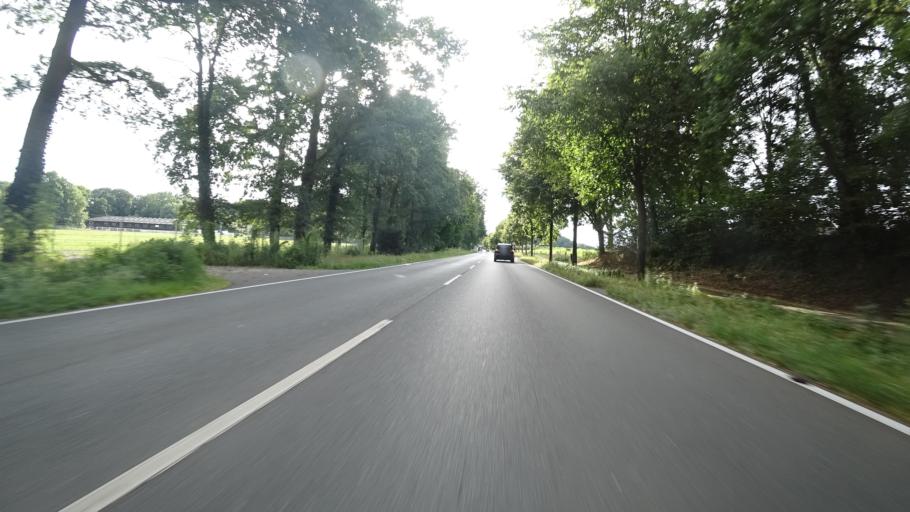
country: DE
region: North Rhine-Westphalia
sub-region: Regierungsbezirk Detmold
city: Harsewinkel
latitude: 51.9647
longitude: 8.2002
